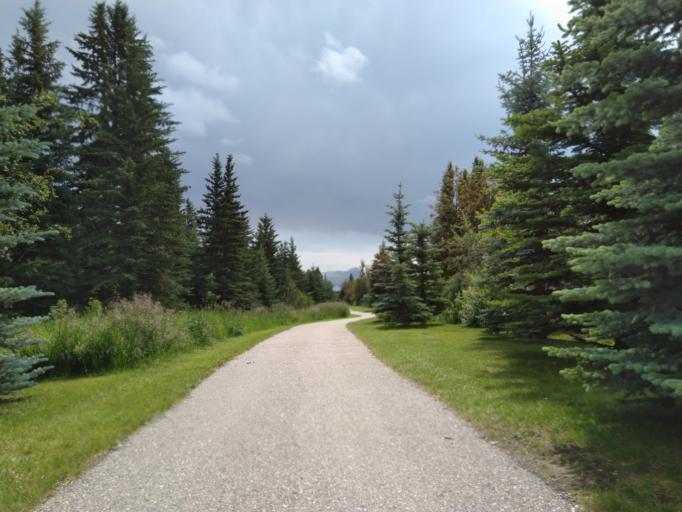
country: CA
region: Alberta
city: Cochrane
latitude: 51.1876
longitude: -114.5075
